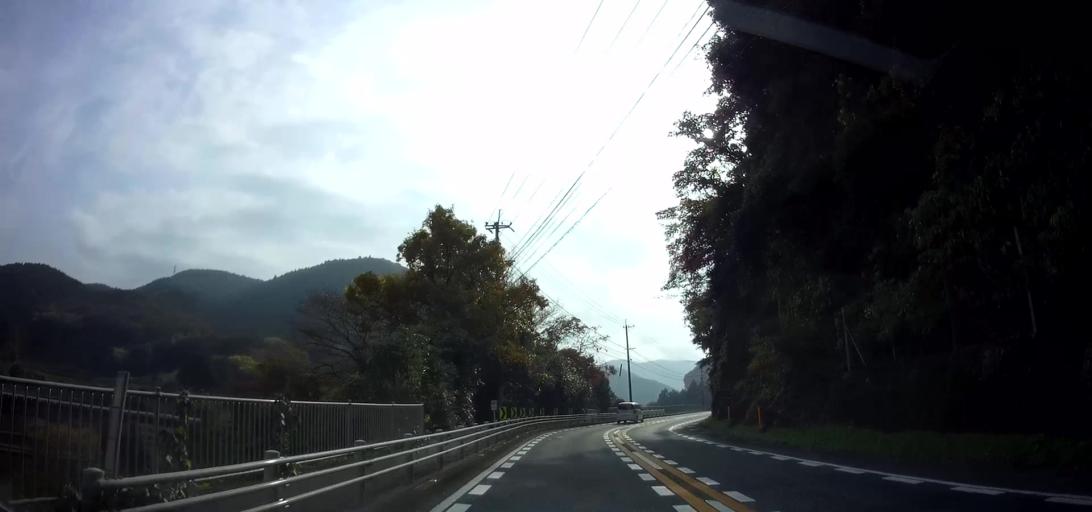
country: JP
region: Nagasaki
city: Shimabara
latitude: 32.7792
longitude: 130.2094
